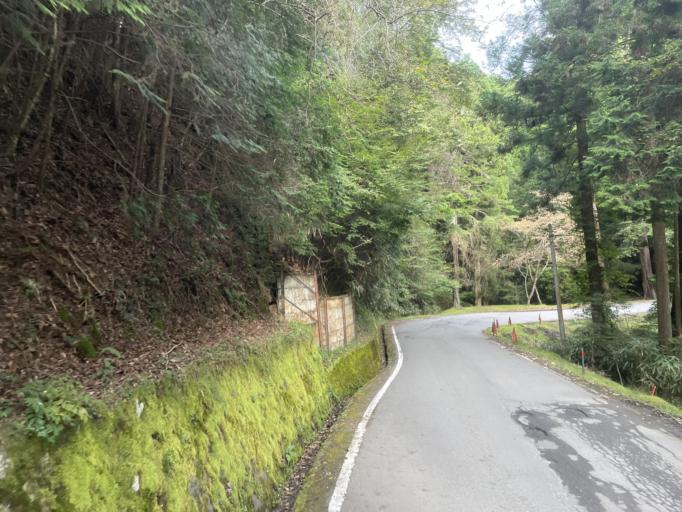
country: JP
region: Wakayama
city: Koya
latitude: 34.2254
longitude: 135.5760
